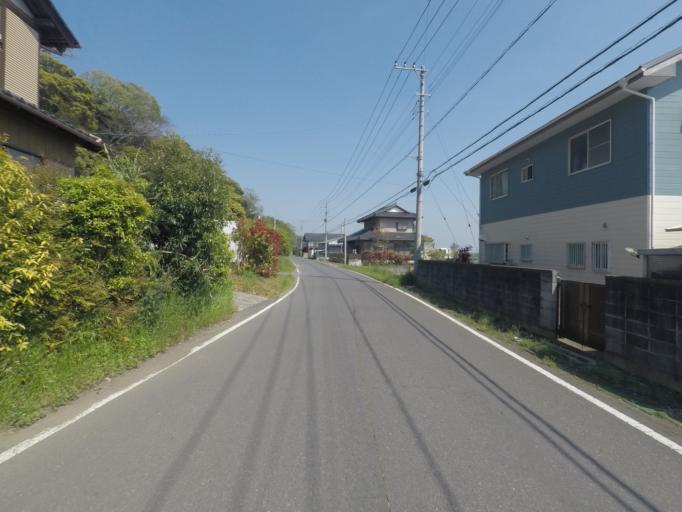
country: JP
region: Ibaraki
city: Ami
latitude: 36.0734
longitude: 140.2694
